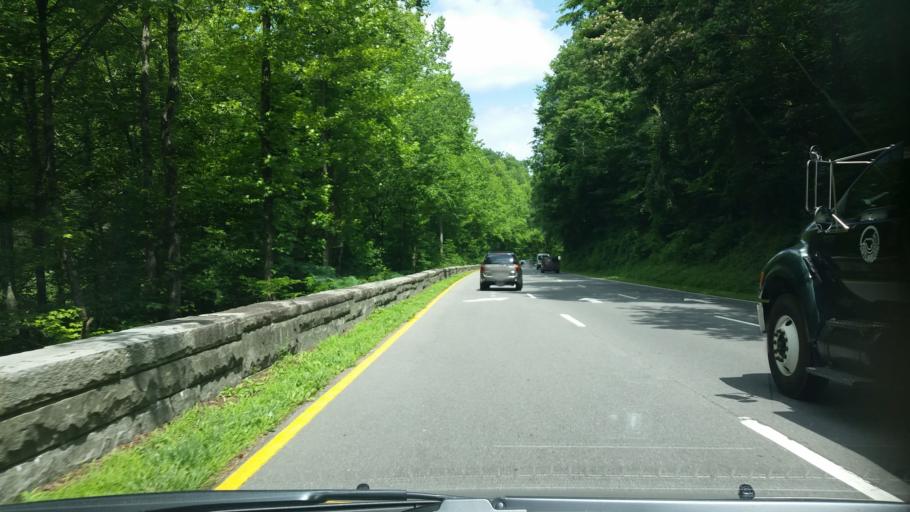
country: US
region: Tennessee
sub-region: Sevier County
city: Gatlinburg
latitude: 35.7273
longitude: -83.5172
